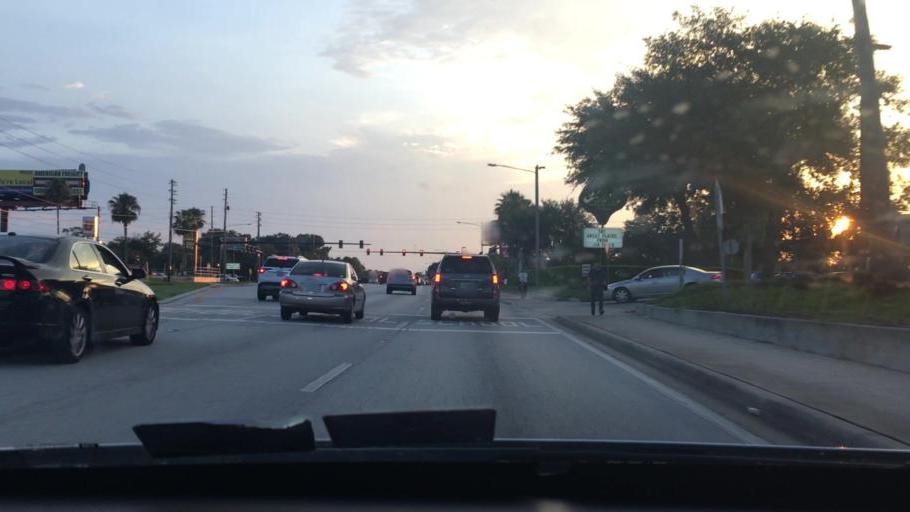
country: US
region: Florida
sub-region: Seminole County
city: Goldenrod
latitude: 28.5976
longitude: -81.2974
